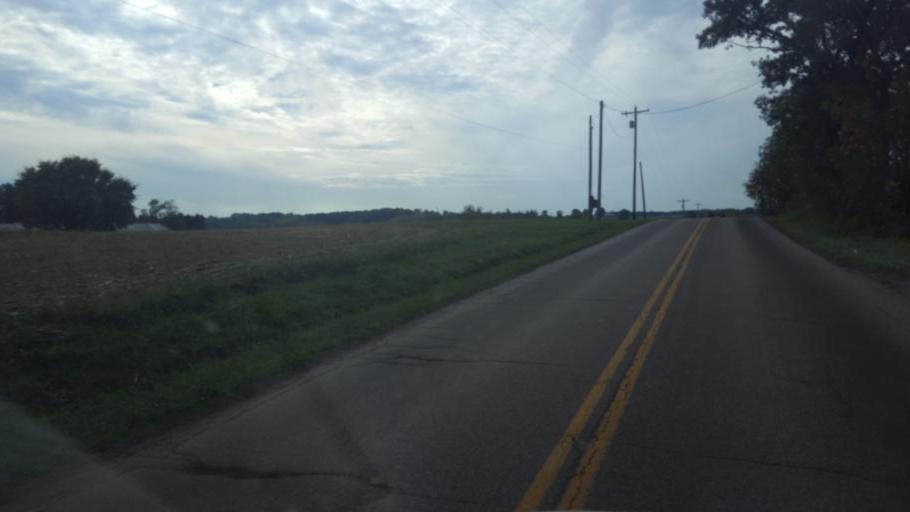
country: US
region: Ohio
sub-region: Holmes County
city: Millersburg
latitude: 40.5873
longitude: -81.8259
